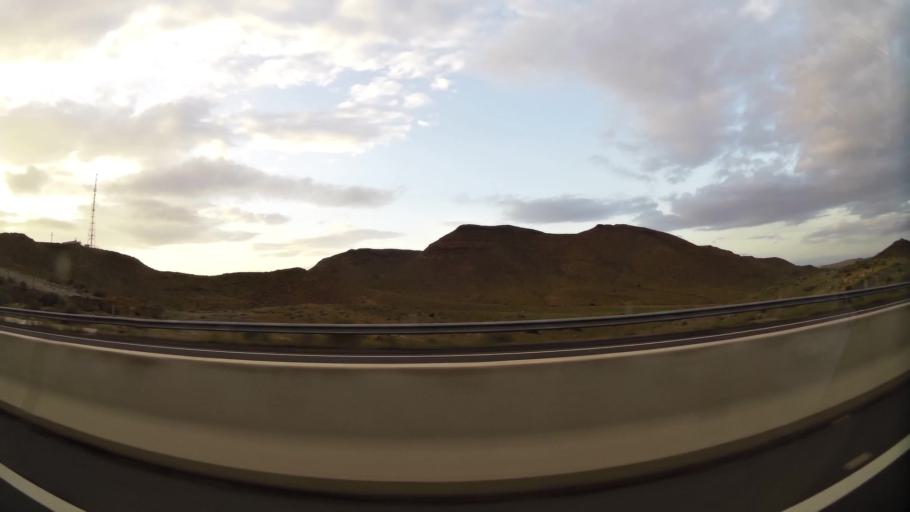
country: MA
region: Oriental
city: Taourirt
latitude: 34.4658
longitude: -3.0136
